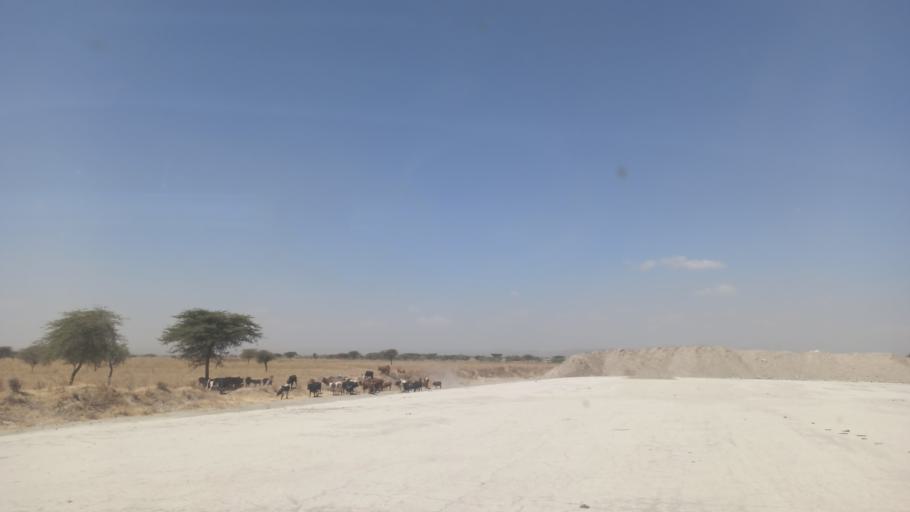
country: ET
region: Oromiya
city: Ziway
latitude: 7.7304
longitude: 38.6257
